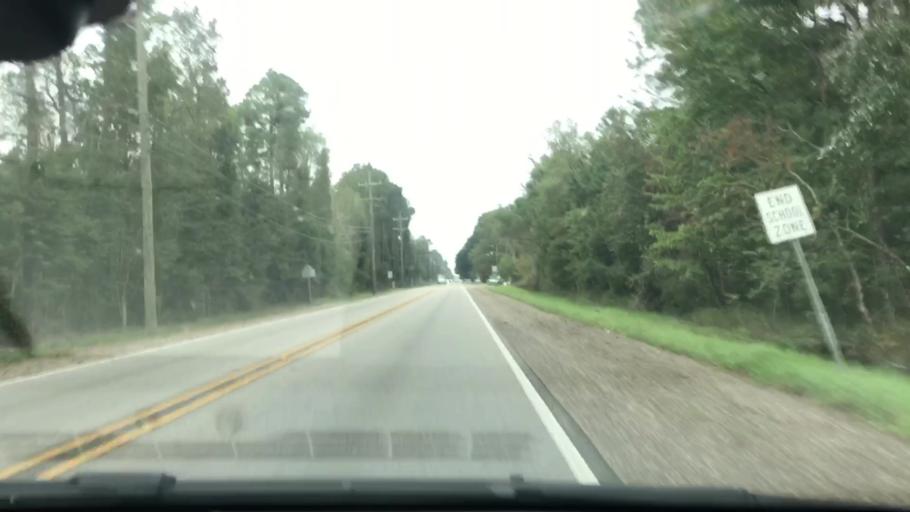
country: US
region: Louisiana
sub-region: Saint Tammany Parish
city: Pearl River
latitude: 30.3336
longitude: -89.7614
